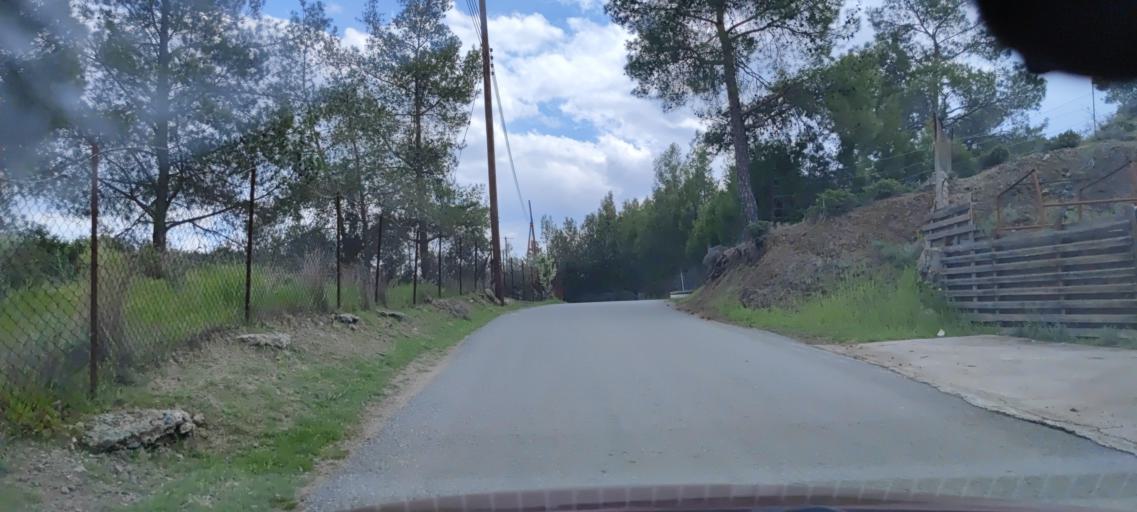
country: CY
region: Lefkosia
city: Lythrodontas
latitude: 34.9410
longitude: 33.3135
